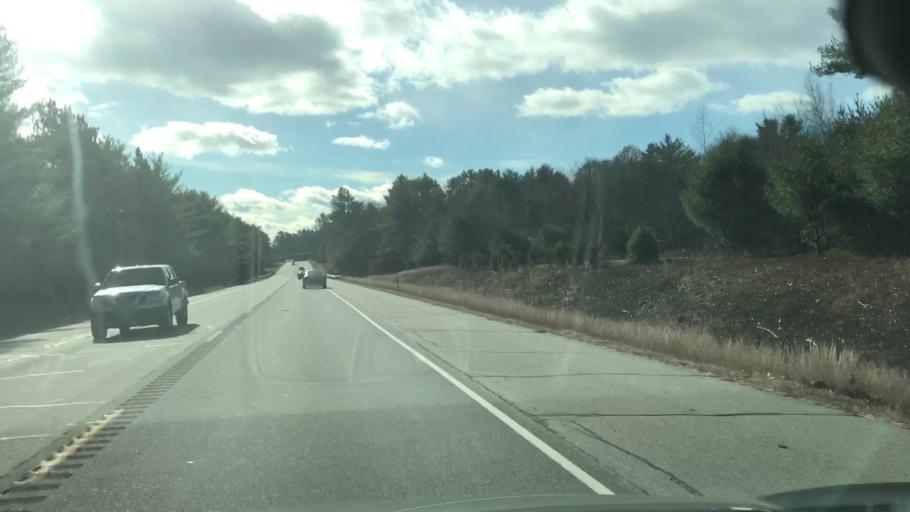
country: US
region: New Hampshire
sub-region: Merrimack County
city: Chichester
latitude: 43.2786
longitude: -71.3648
